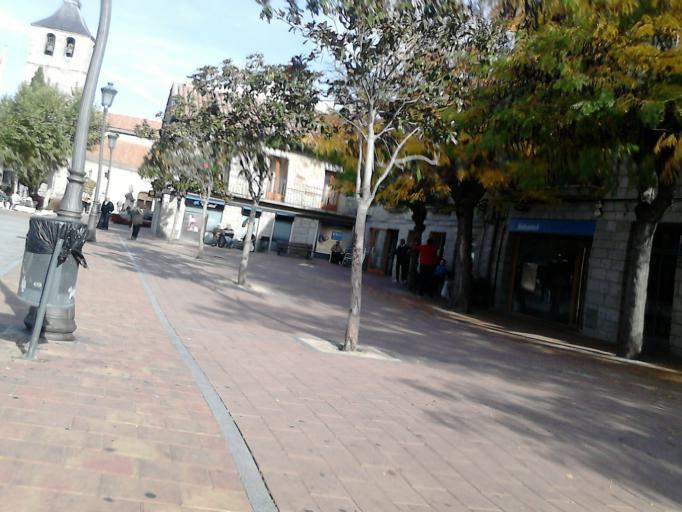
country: ES
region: Madrid
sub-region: Provincia de Madrid
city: Galapagar
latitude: 40.5774
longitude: -4.0036
